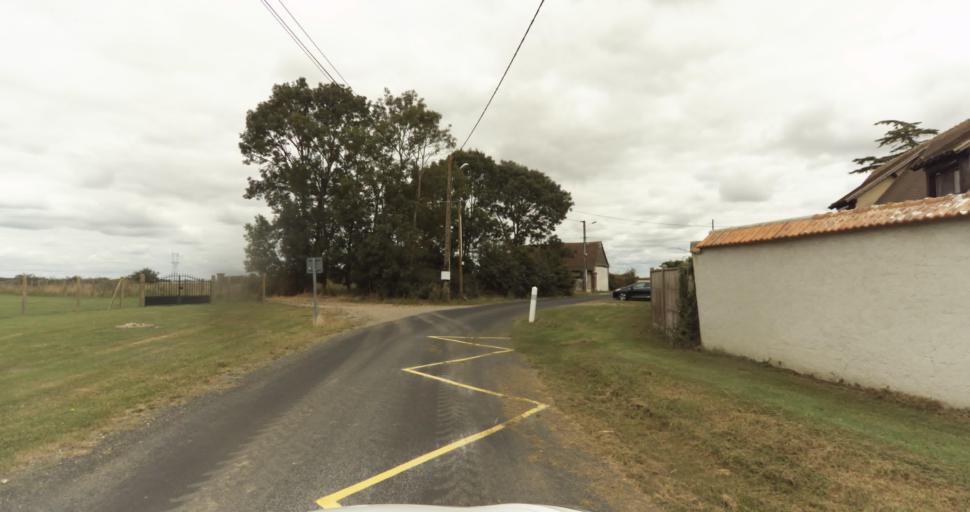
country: FR
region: Haute-Normandie
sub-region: Departement de l'Eure
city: La Madeleine-de-Nonancourt
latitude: 48.8445
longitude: 1.1910
